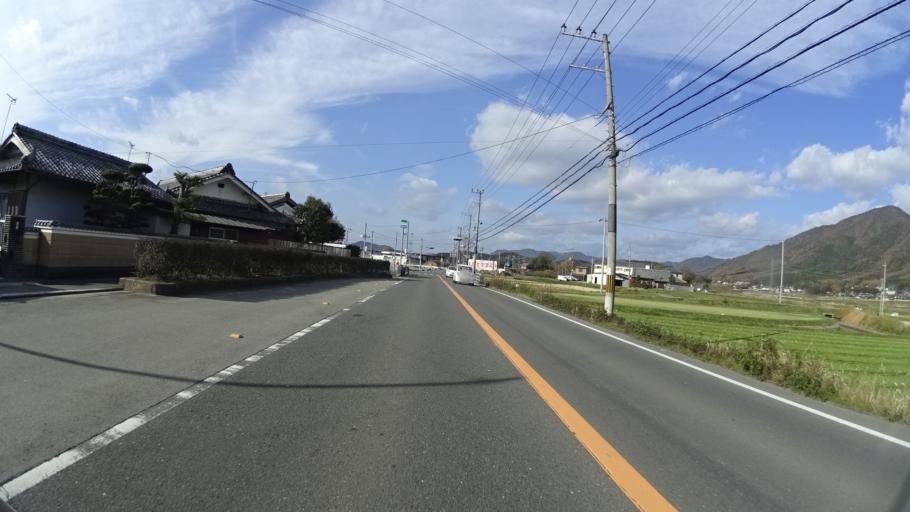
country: JP
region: Kyoto
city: Kameoka
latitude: 35.0540
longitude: 135.5713
